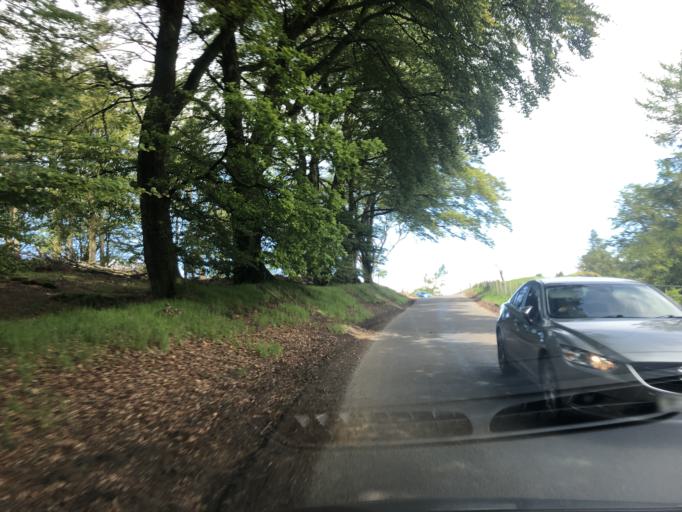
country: GB
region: Scotland
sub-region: Angus
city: Kirriemuir
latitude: 56.7660
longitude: -3.0201
